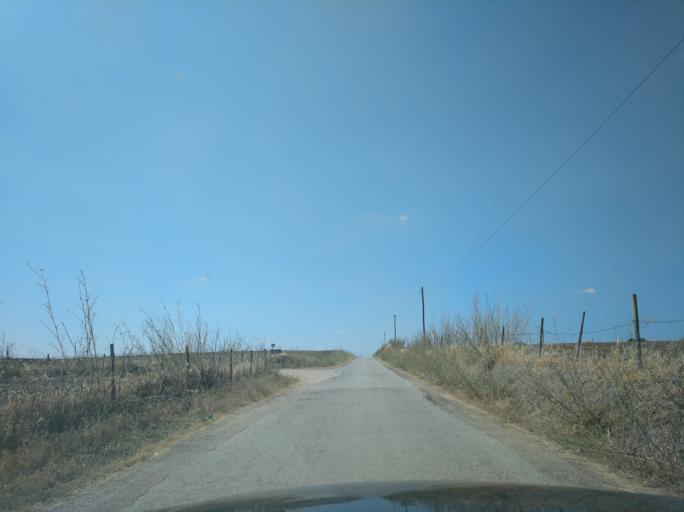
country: PT
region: Portalegre
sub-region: Campo Maior
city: Campo Maior
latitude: 39.0214
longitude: -7.0829
